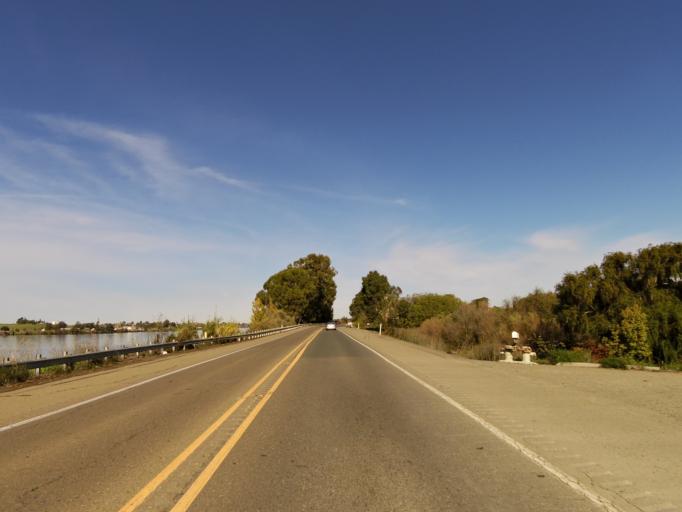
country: US
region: California
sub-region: Solano County
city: Rio Vista
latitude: 38.1358
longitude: -121.6861
